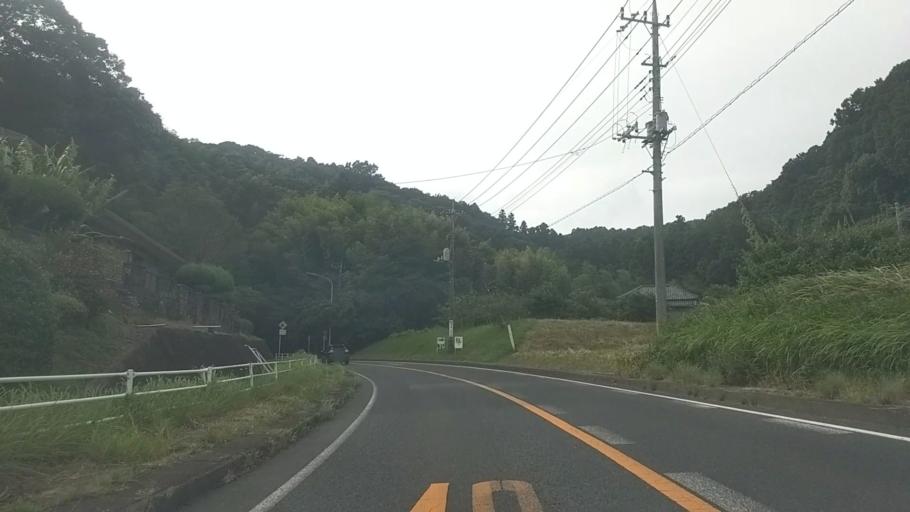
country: JP
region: Chiba
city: Kimitsu
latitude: 35.3136
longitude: 139.9610
